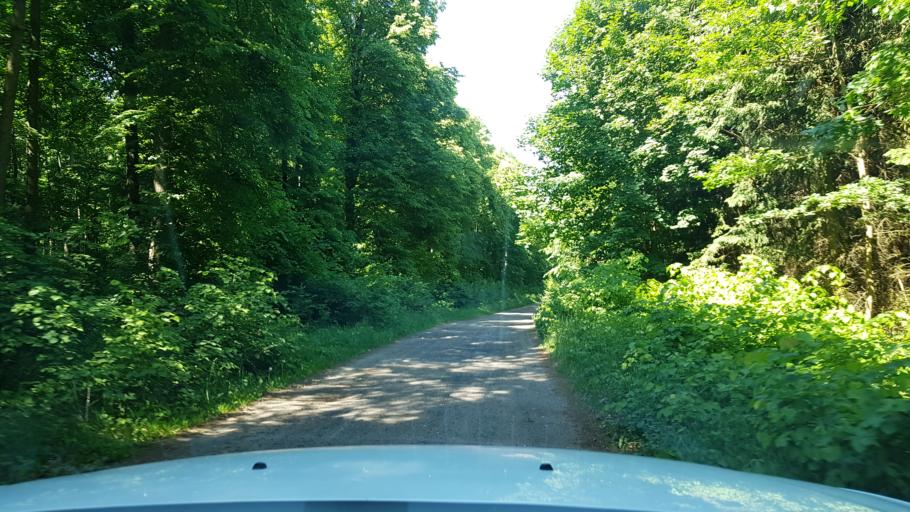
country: PL
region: West Pomeranian Voivodeship
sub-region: Powiat gryfinski
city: Banie
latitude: 53.1138
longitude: 14.5397
